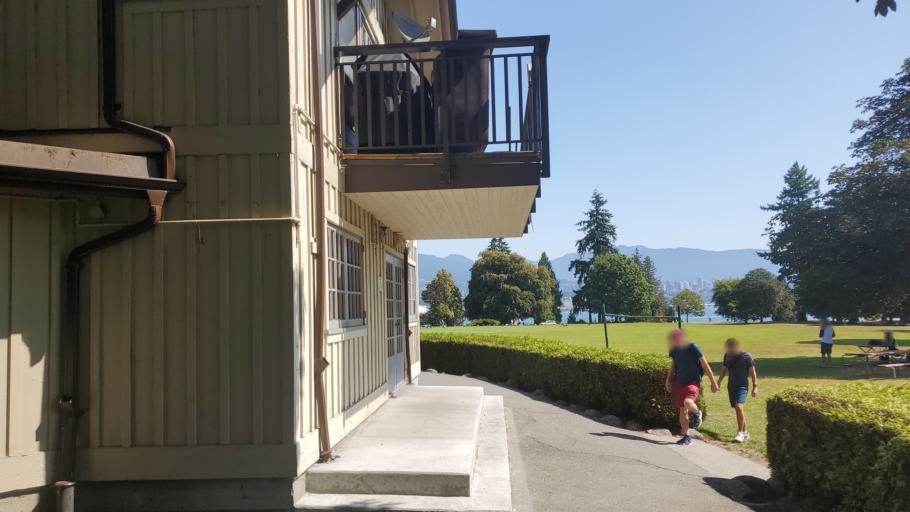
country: CA
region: British Columbia
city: West End
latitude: 49.2990
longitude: -123.1244
